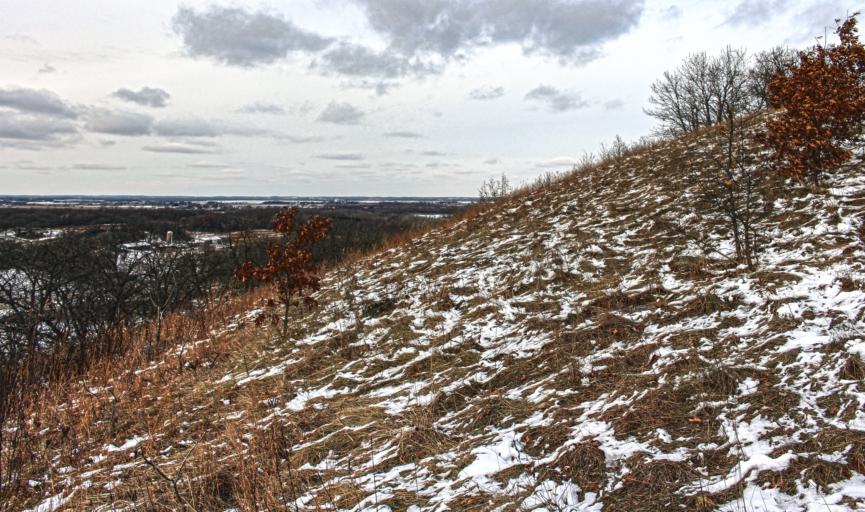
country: US
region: Wisconsin
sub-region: Jefferson County
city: Palmyra
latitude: 42.8443
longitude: -88.6069
